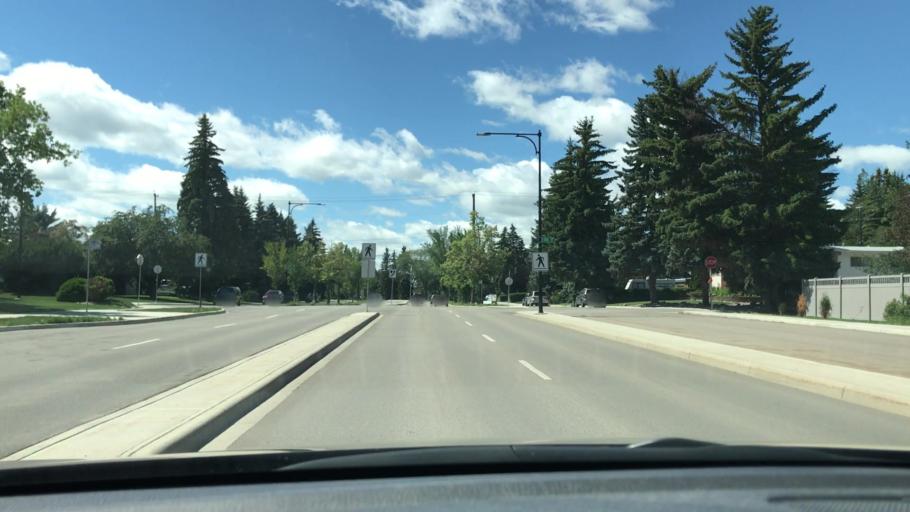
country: CA
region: Alberta
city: Edmonton
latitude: 53.5194
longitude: -113.5617
